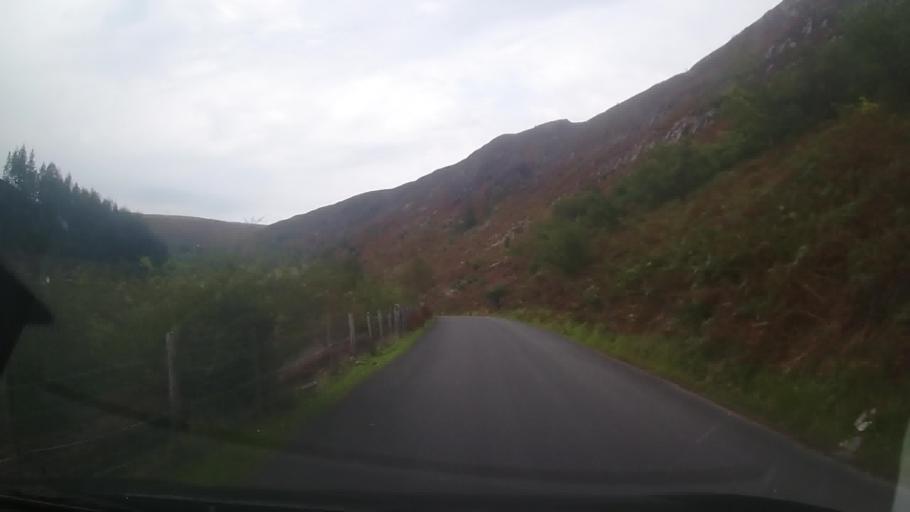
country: GB
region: Wales
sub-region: Sir Powys
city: Rhayader
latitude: 52.2850
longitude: -3.5931
